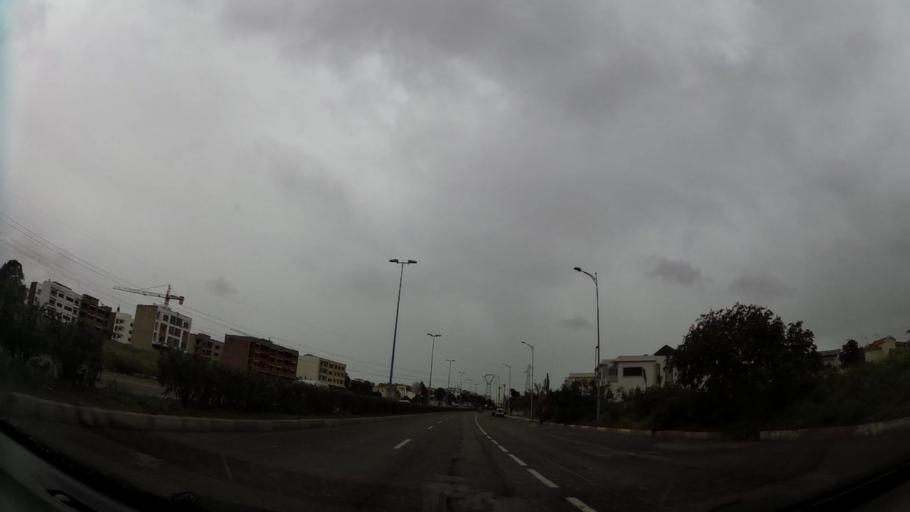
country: MA
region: Grand Casablanca
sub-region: Casablanca
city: Casablanca
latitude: 33.5393
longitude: -7.6180
